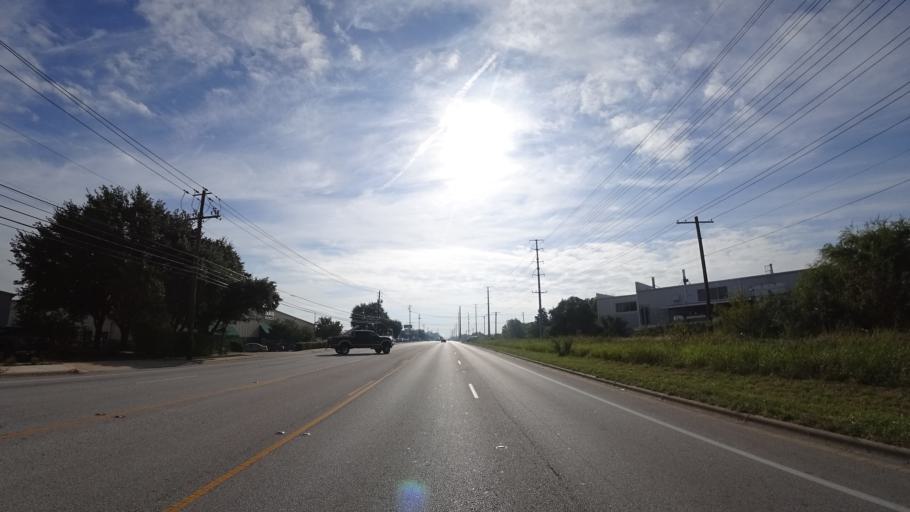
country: US
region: Texas
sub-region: Travis County
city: Austin
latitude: 30.2112
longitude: -97.7285
